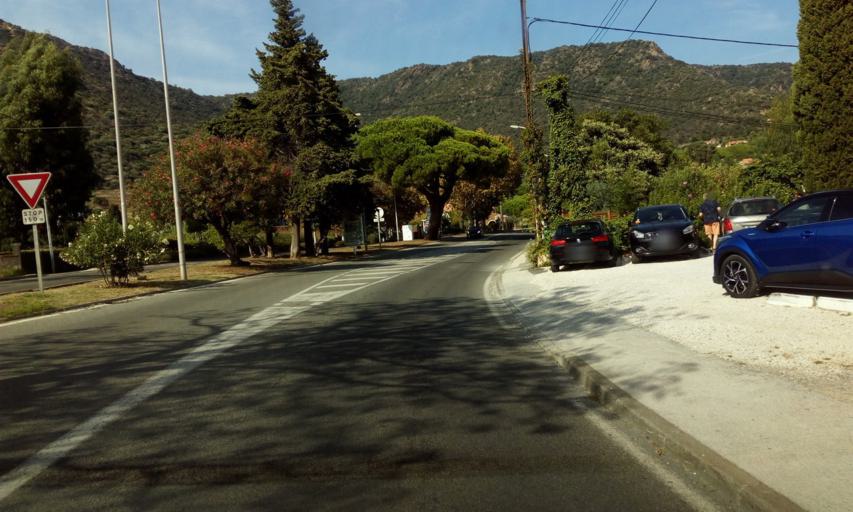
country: FR
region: Provence-Alpes-Cote d'Azur
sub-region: Departement du Var
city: Le Lavandou
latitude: 43.1434
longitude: 6.3792
